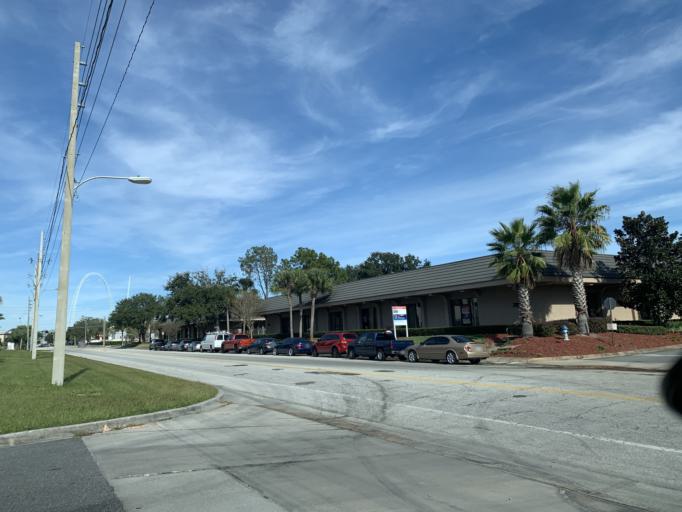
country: US
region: Florida
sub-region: Orange County
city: Tangelo Park
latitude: 28.4597
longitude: -81.4563
